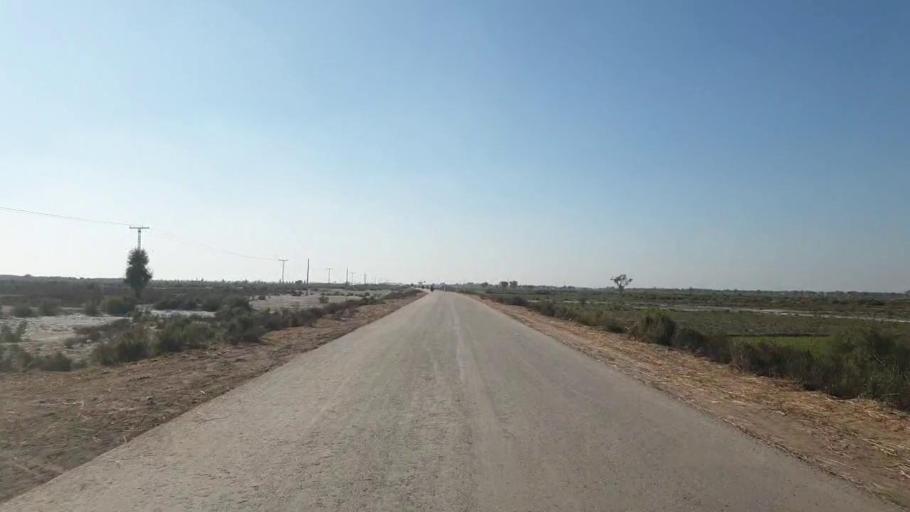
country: PK
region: Sindh
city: New Badah
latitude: 27.3248
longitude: 68.0625
